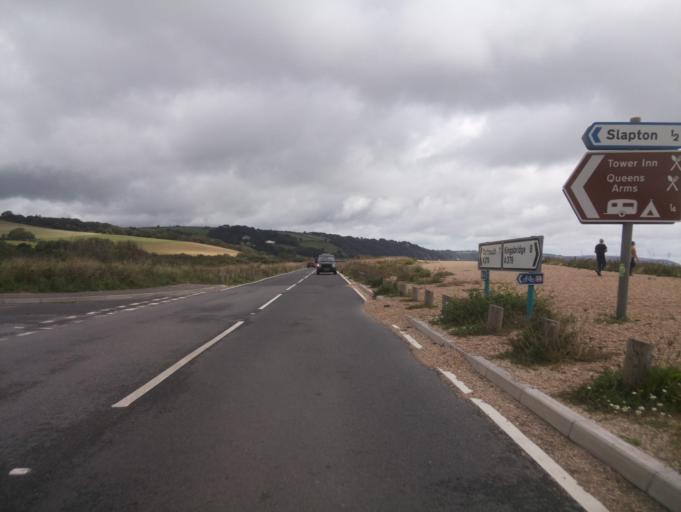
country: GB
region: England
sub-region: Devon
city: Dartmouth
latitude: 50.2875
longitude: -3.6451
